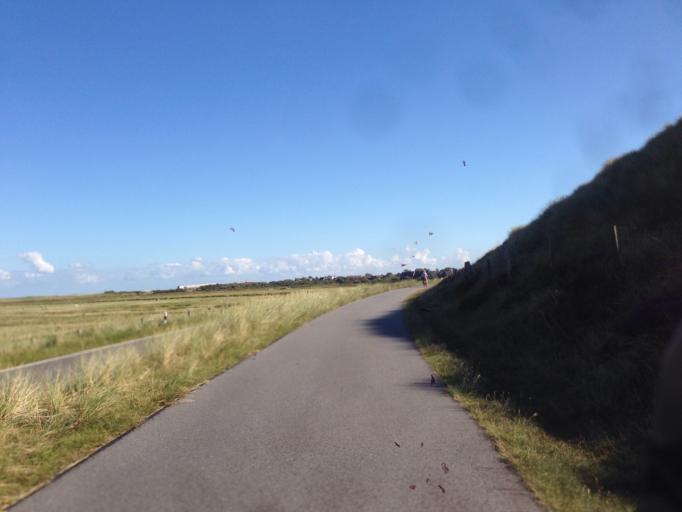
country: DE
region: Schleswig-Holstein
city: List
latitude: 55.0288
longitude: 8.4174
